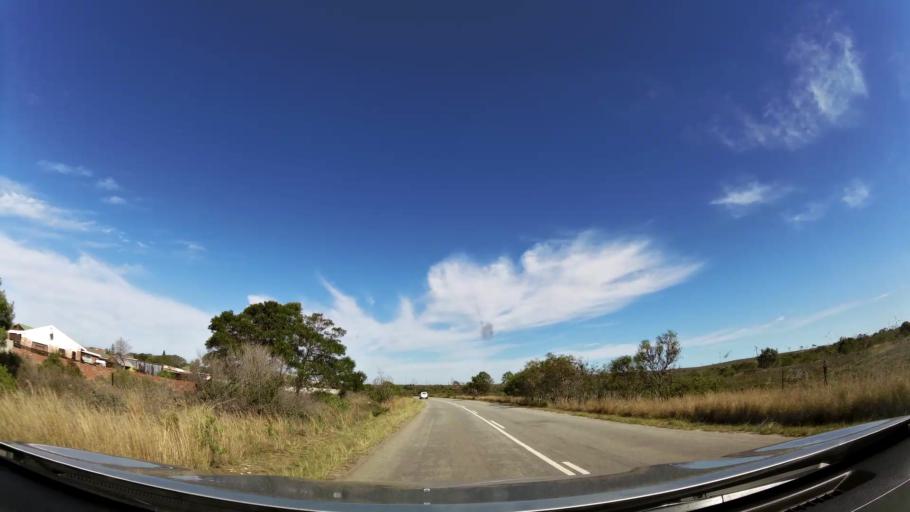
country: ZA
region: Eastern Cape
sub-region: Cacadu District Municipality
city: Jeffrey's Bay
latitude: -34.0239
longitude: 24.9060
